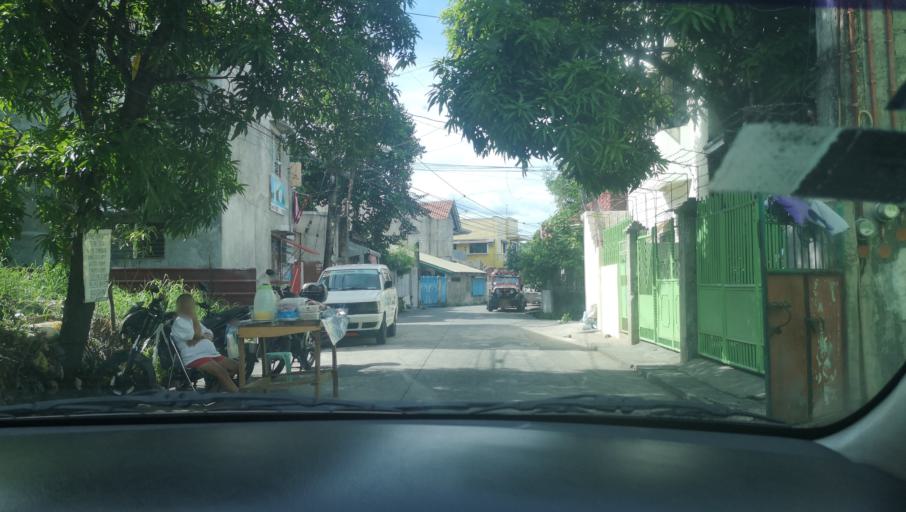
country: PH
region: Calabarzon
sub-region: Province of Rizal
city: San Mateo
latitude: 14.6759
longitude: 121.1155
